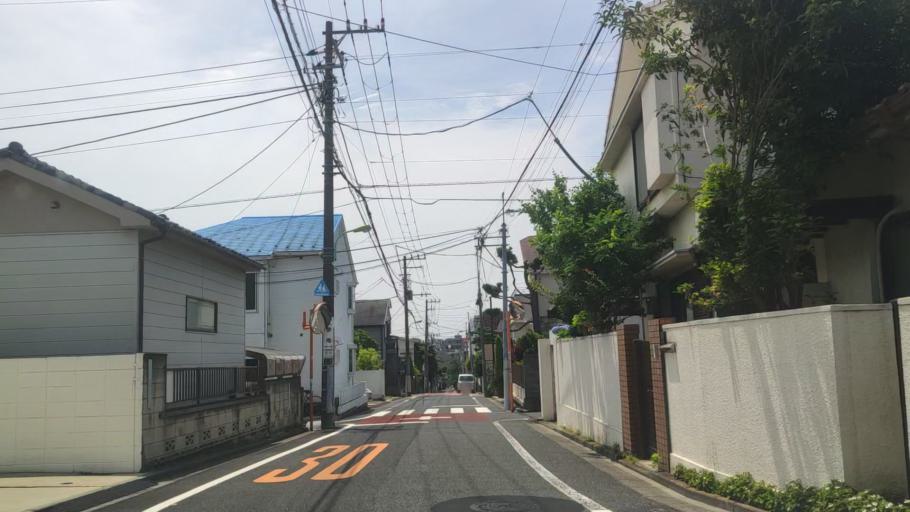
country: JP
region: Tokyo
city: Tokyo
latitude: 35.6566
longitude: 139.6649
